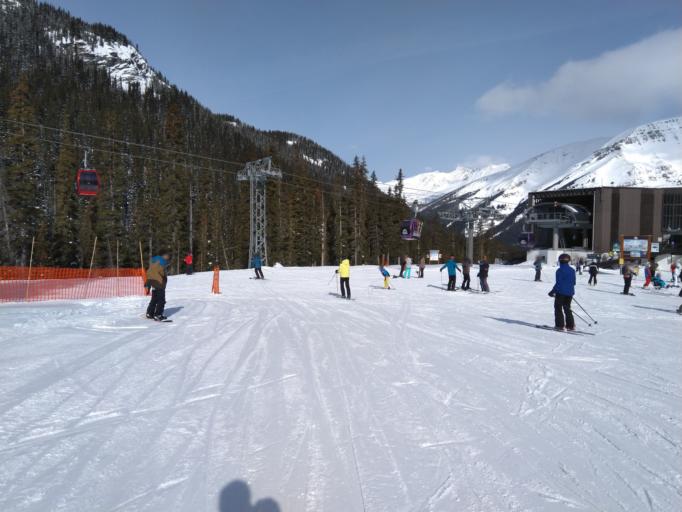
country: CA
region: Alberta
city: Banff
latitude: 51.0949
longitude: -115.7722
